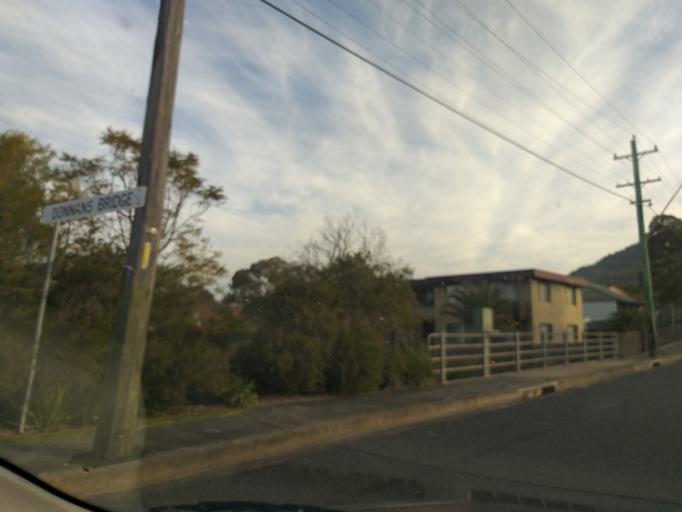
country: AU
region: New South Wales
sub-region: Wollongong
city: Mount Ousley
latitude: -34.3887
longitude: 150.8830
